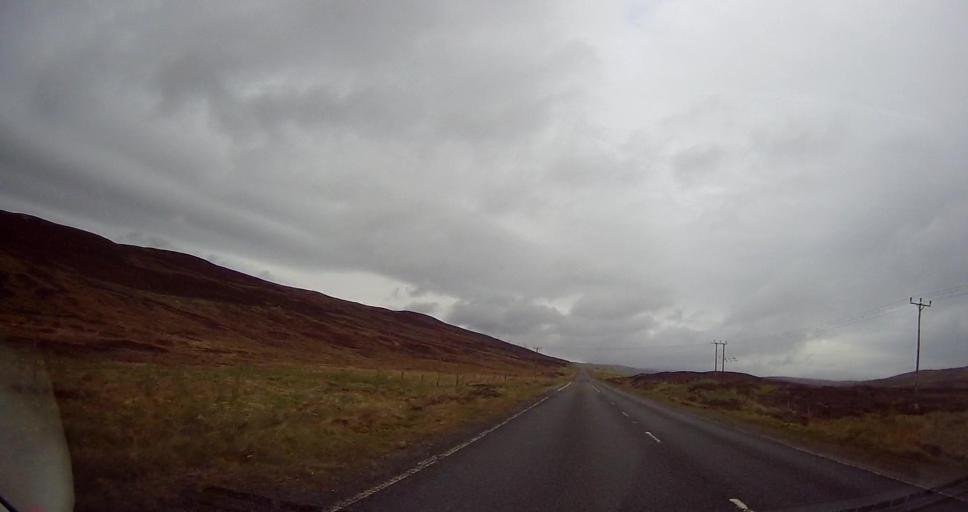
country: GB
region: Scotland
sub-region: Shetland Islands
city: Lerwick
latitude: 60.2094
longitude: -1.2334
